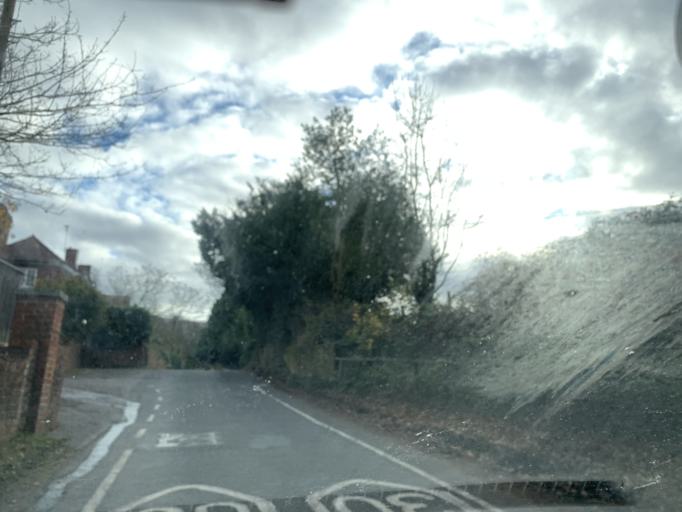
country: GB
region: England
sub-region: Hampshire
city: Lyndhurst
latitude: 50.8754
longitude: -1.5963
